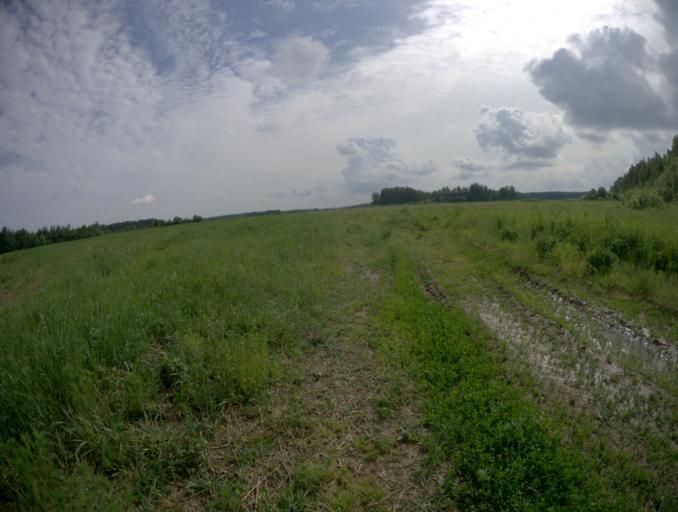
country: RU
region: Vladimir
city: Lakinsk
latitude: 56.0949
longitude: 39.9097
